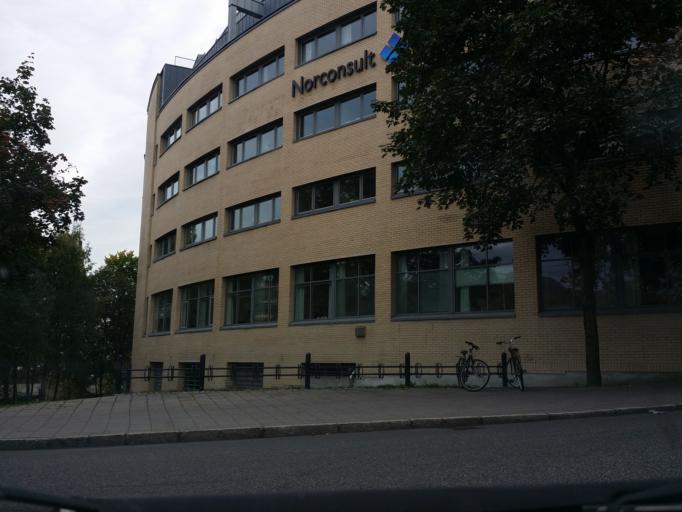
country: NO
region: Akershus
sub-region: Baerum
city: Sandvika
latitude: 59.8911
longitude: 10.5213
